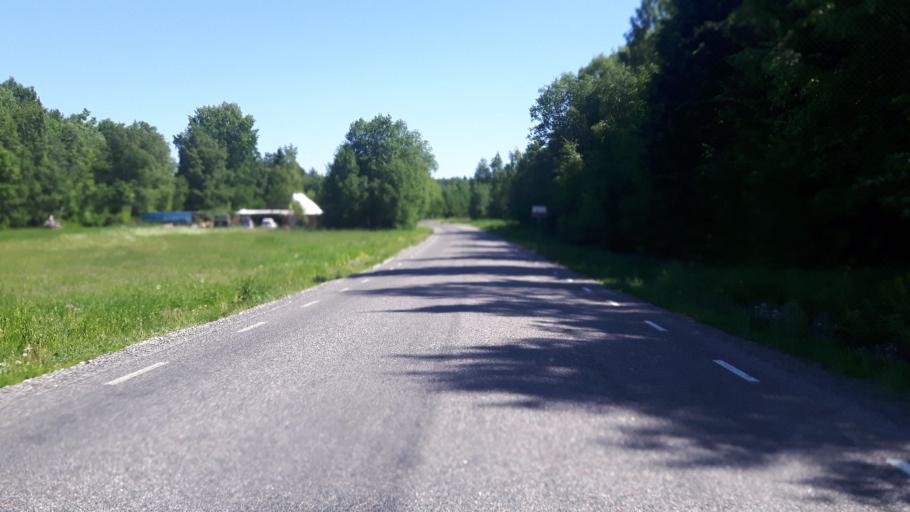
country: EE
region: Raplamaa
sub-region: Kohila vald
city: Kohila
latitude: 59.1811
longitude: 24.7224
